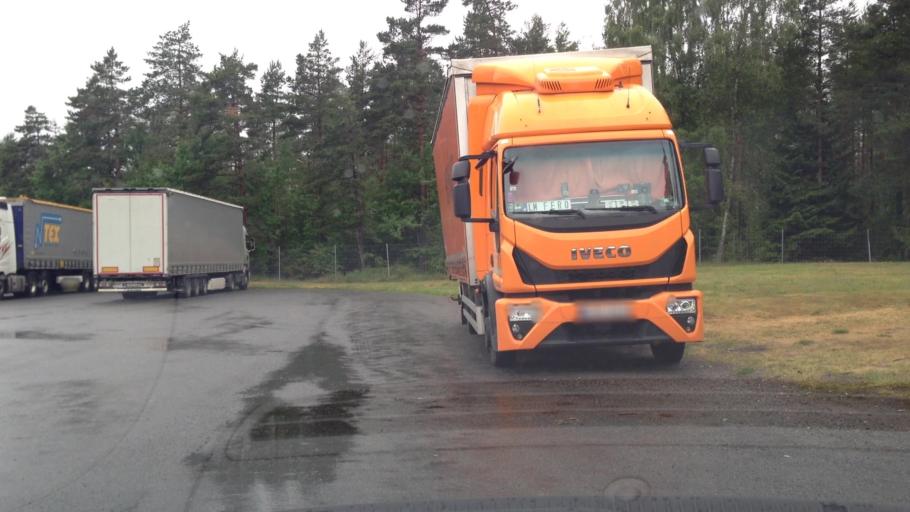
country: SE
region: Joenkoeping
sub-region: Jonkopings Kommun
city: Taberg
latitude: 57.7532
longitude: 13.9512
